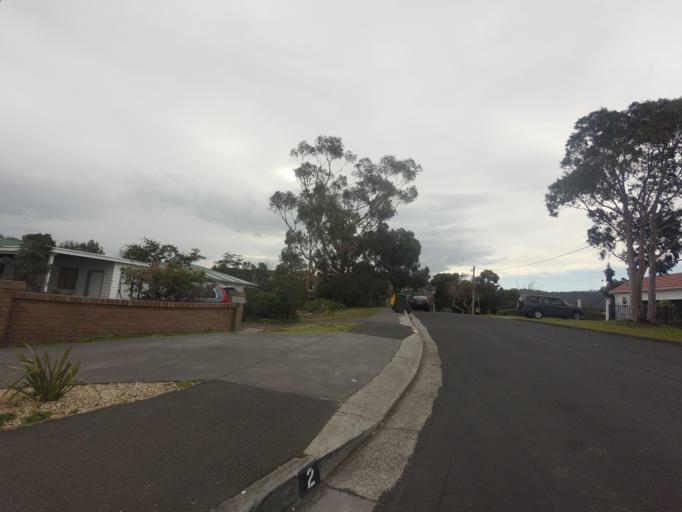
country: AU
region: Tasmania
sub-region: Clarence
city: Bellerive
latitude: -42.8815
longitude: 147.3868
